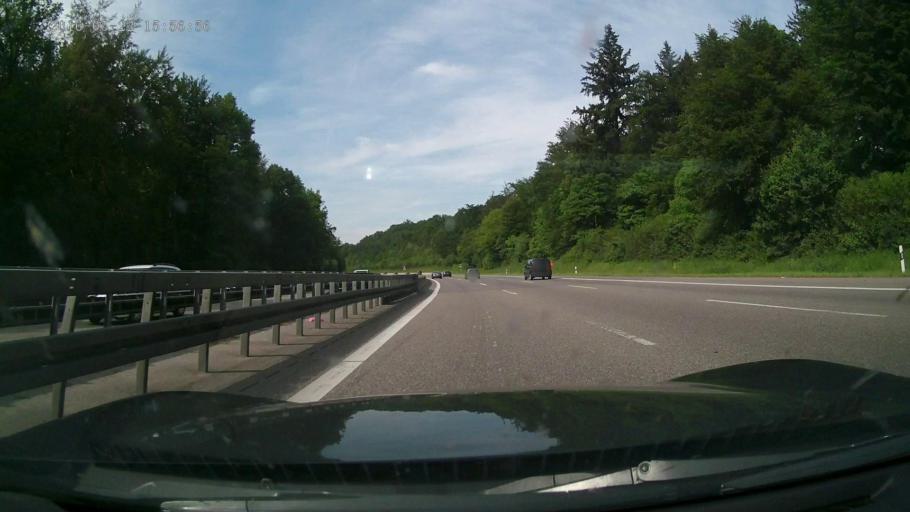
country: DE
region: Baden-Wuerttemberg
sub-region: Regierungsbezirk Stuttgart
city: Untergruppenbach
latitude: 49.1058
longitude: 9.3019
